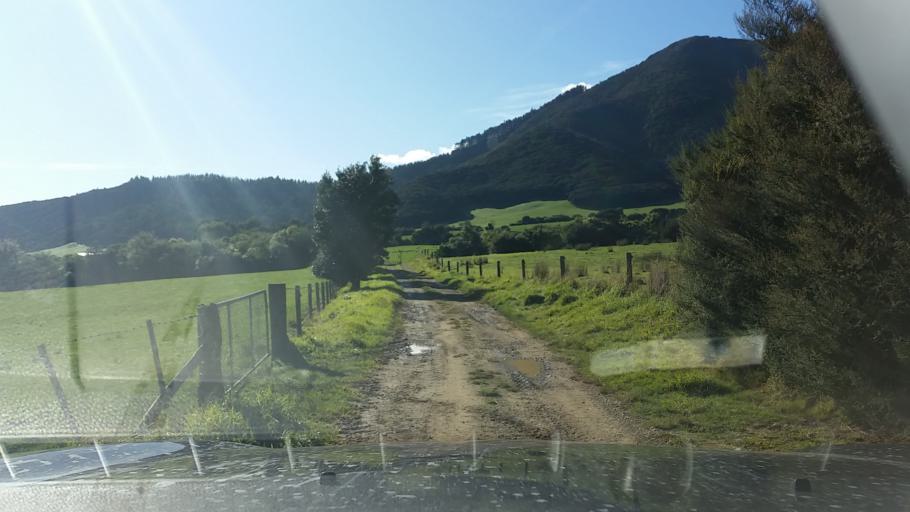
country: NZ
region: Marlborough
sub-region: Marlborough District
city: Picton
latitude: -41.1148
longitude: 173.9914
